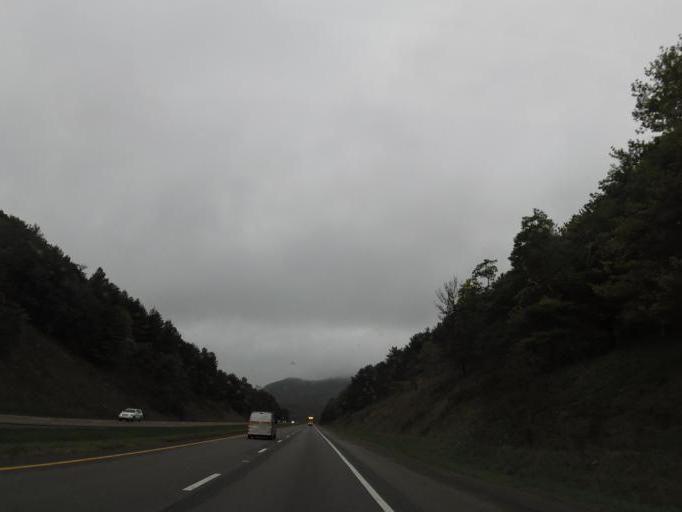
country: US
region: Virginia
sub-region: Wythe County
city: Wytheville
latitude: 37.0131
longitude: -81.1059
